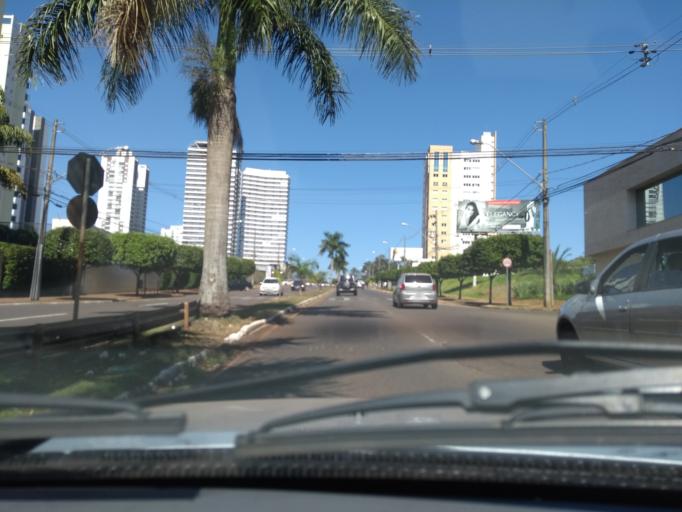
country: BR
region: Parana
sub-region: Londrina
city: Londrina
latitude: -23.3323
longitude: -51.1775
